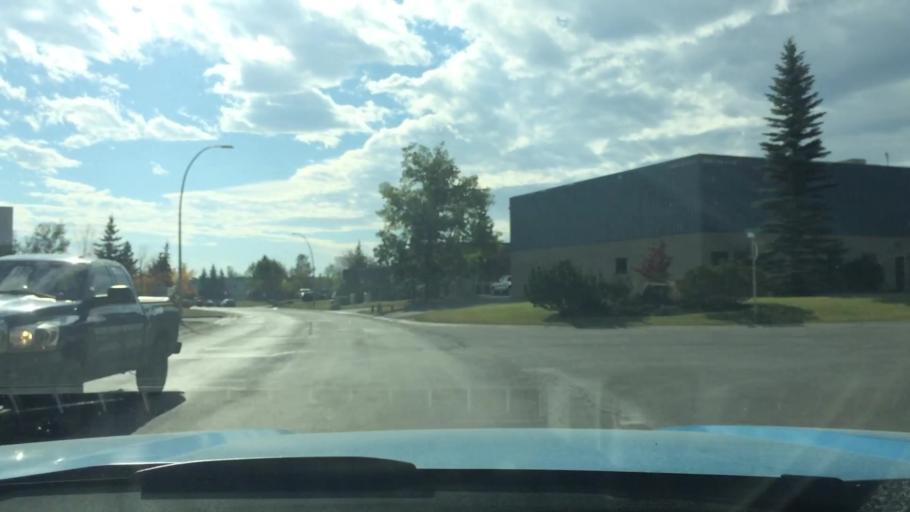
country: CA
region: Alberta
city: Calgary
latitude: 51.0101
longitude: -114.0347
